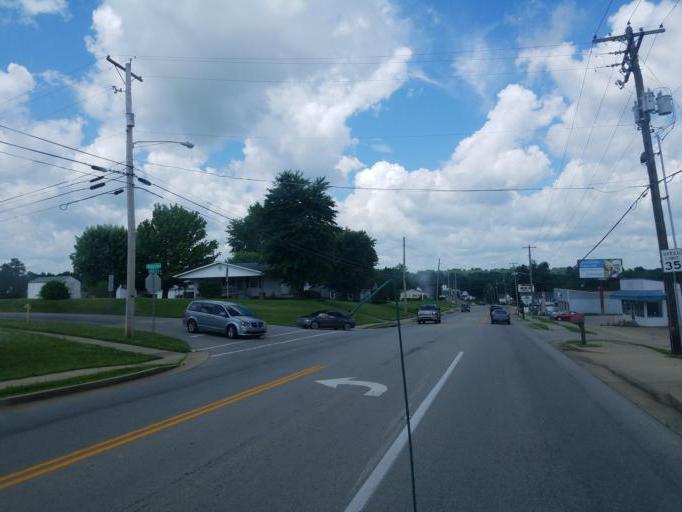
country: US
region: Kentucky
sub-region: Grayson County
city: Leitchfield
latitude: 37.4839
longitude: -86.2834
